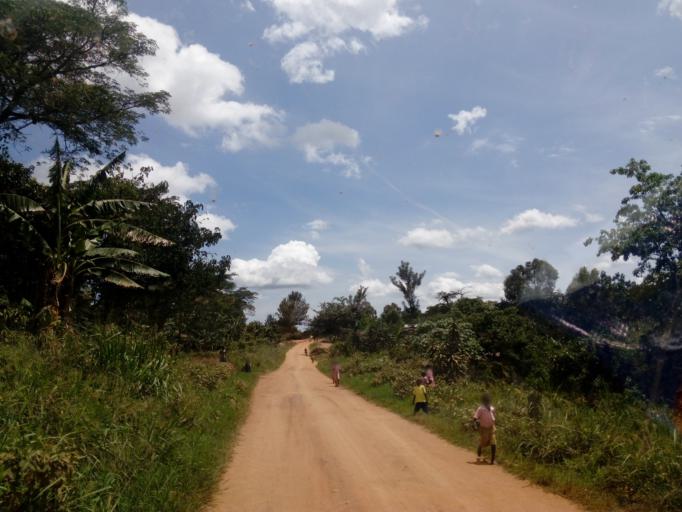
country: UG
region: Central Region
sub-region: Mubende District
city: Mubende
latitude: 0.4582
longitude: 31.6966
